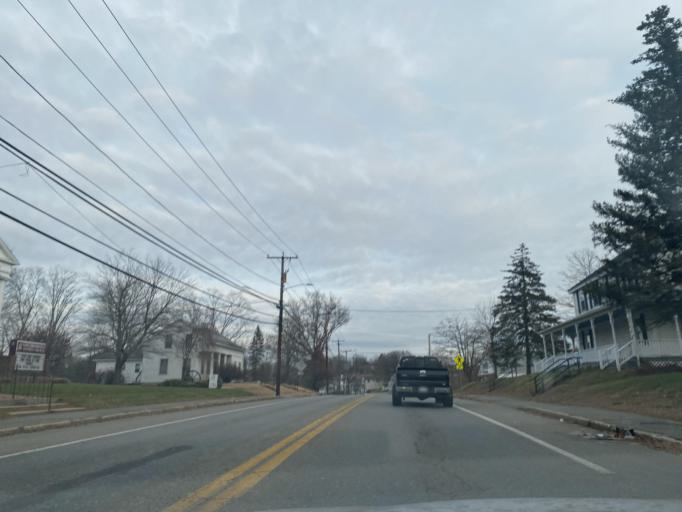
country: US
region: Massachusetts
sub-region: Worcester County
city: East Brookfield
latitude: 42.2264
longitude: -72.0517
